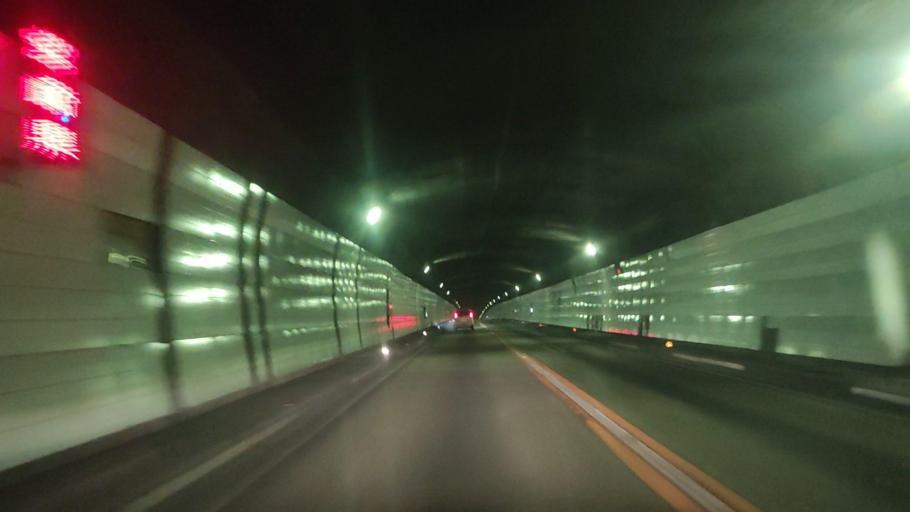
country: JP
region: Kumamoto
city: Hitoyoshi
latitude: 32.0984
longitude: 130.8036
